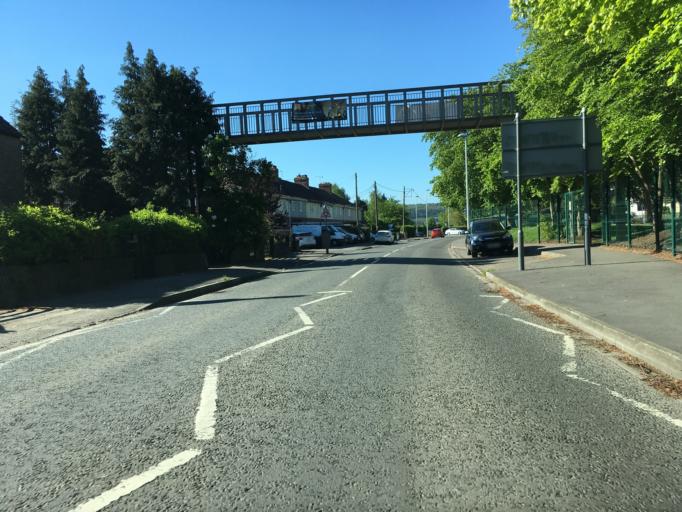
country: GB
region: England
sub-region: North Somerset
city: Portishead
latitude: 51.4752
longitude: -2.7690
